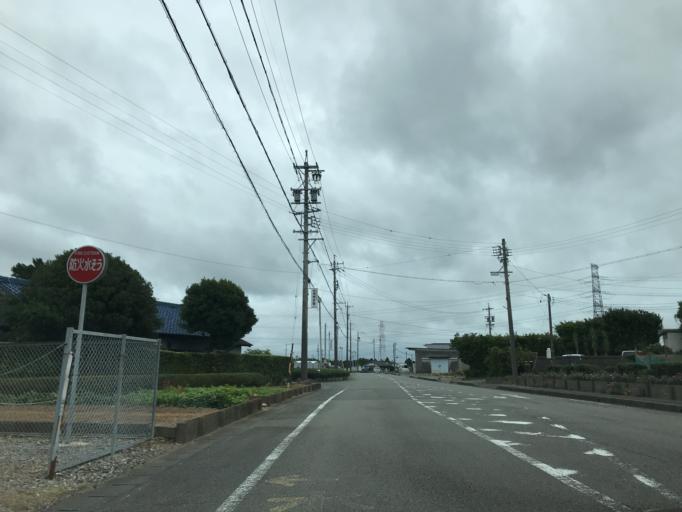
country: JP
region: Shizuoka
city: Sagara
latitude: 34.6977
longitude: 138.1445
